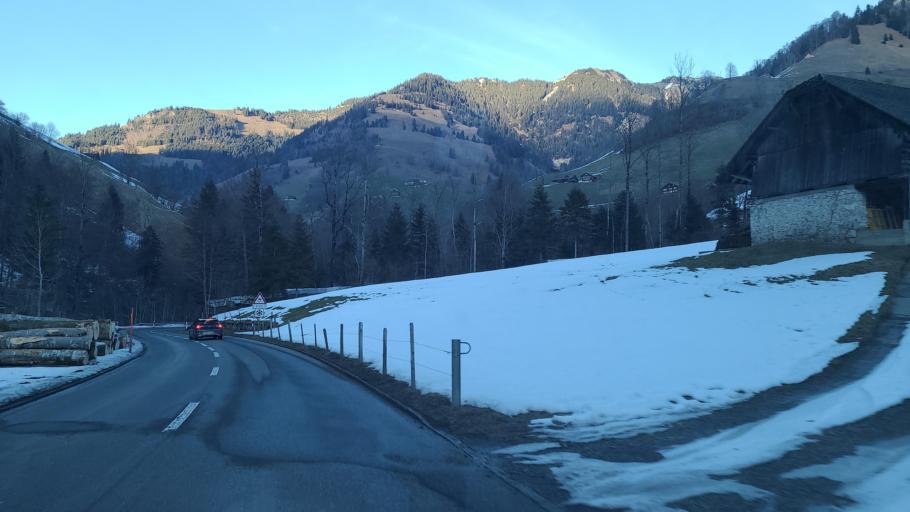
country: CH
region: Obwalden
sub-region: Obwalden
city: Kerns
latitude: 46.8451
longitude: 8.2961
